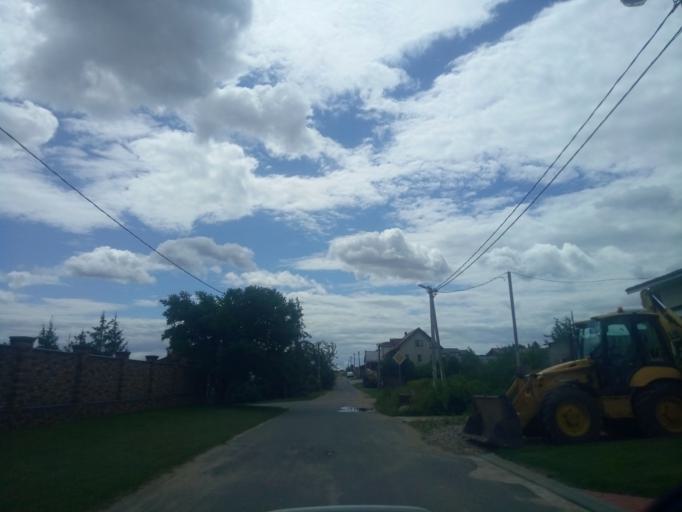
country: BY
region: Minsk
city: Zhdanovichy
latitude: 53.9387
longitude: 27.4023
